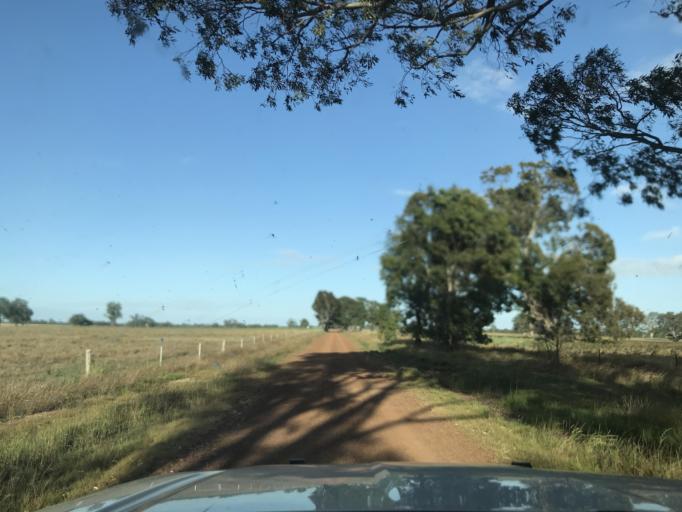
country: AU
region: South Australia
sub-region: Naracoorte and Lucindale
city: Naracoorte
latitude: -36.9569
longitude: 141.3791
